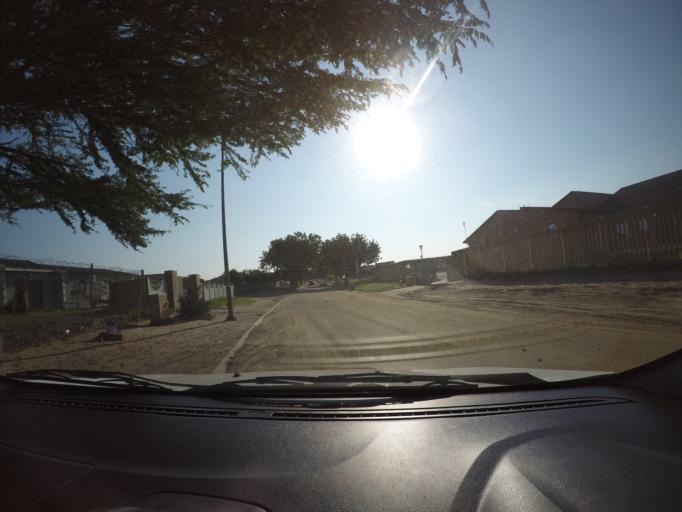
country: ZA
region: KwaZulu-Natal
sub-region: uThungulu District Municipality
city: Richards Bay
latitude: -28.7139
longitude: 32.0337
